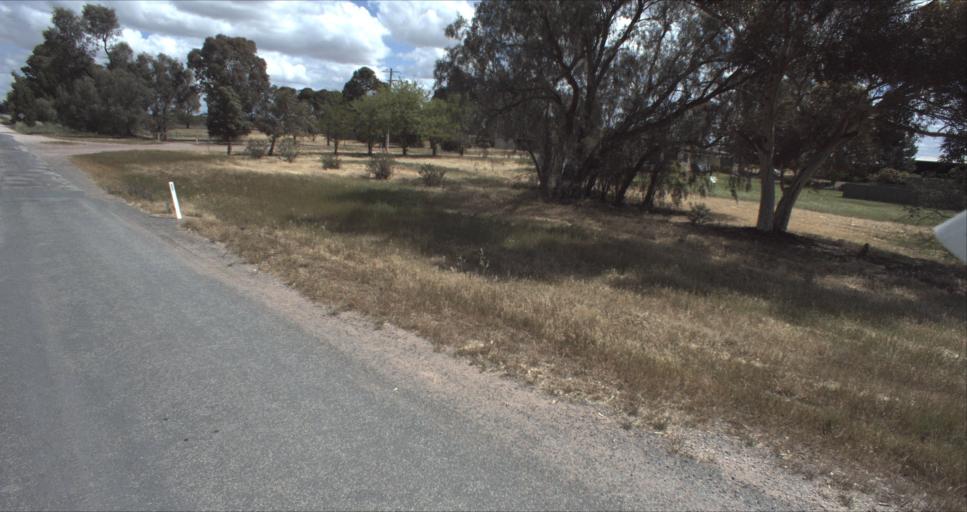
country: AU
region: New South Wales
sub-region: Leeton
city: Leeton
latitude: -34.5880
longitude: 146.3614
